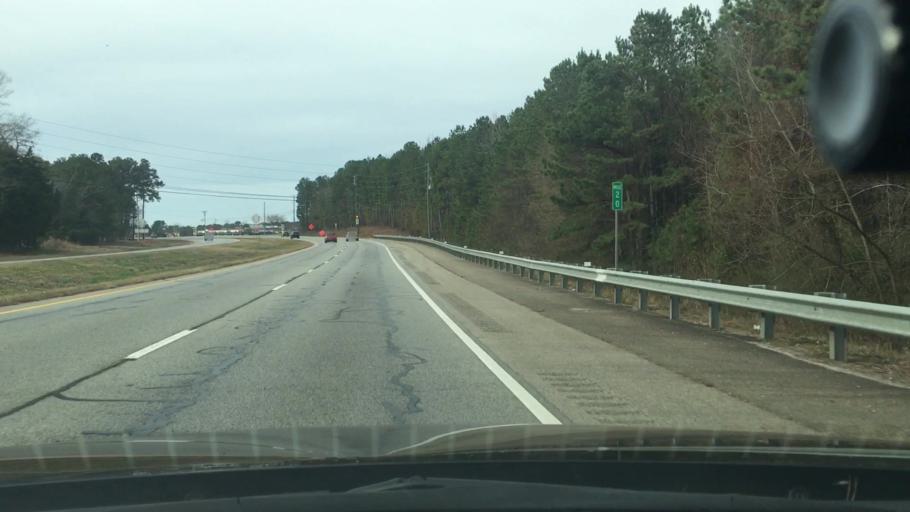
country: US
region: Georgia
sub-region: Fayette County
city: Peachtree City
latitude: 33.4048
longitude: -84.6653
